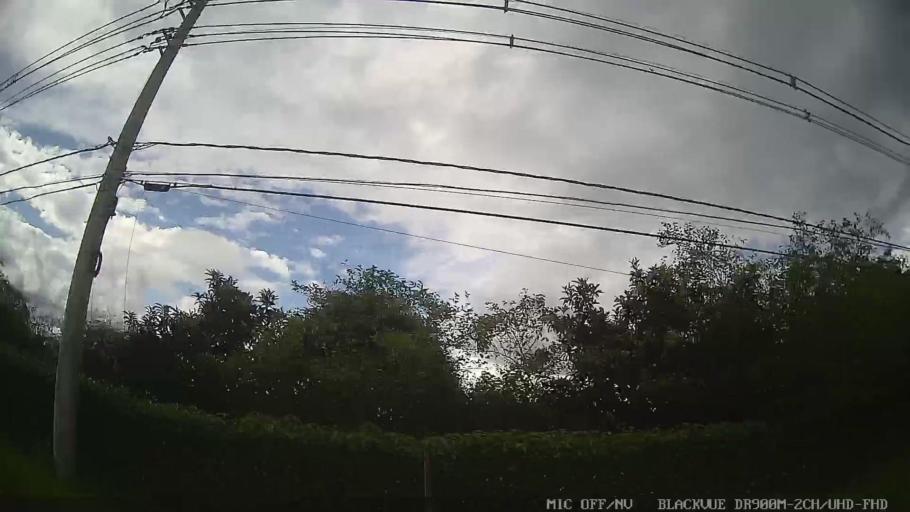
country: BR
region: Sao Paulo
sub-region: Biritiba-Mirim
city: Biritiba Mirim
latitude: -23.5661
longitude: -46.0770
